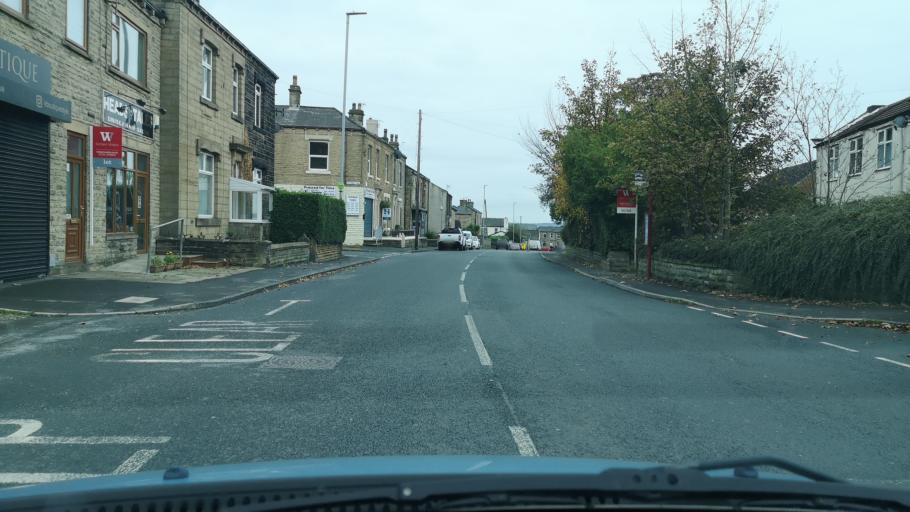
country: GB
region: England
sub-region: Kirklees
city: Heckmondwike
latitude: 53.7286
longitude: -1.6828
